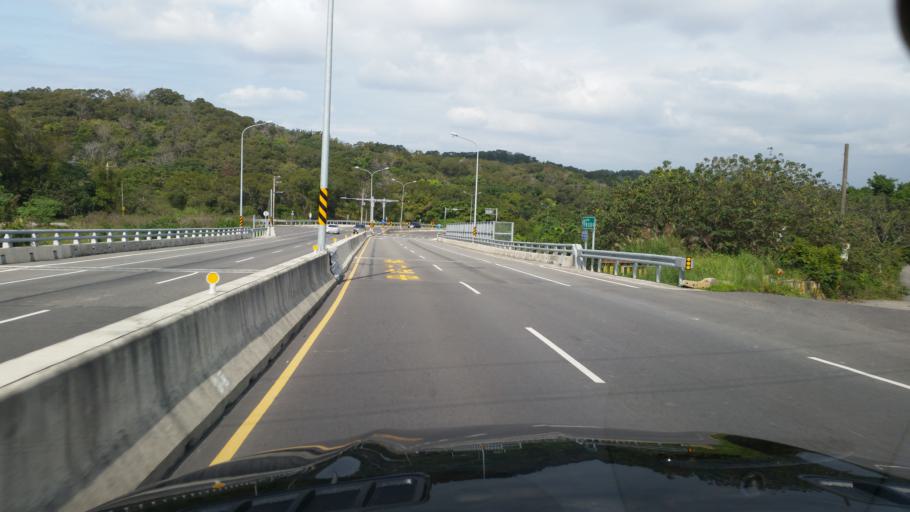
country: TW
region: Taiwan
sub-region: Miaoli
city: Miaoli
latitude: 24.6272
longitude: 120.8529
